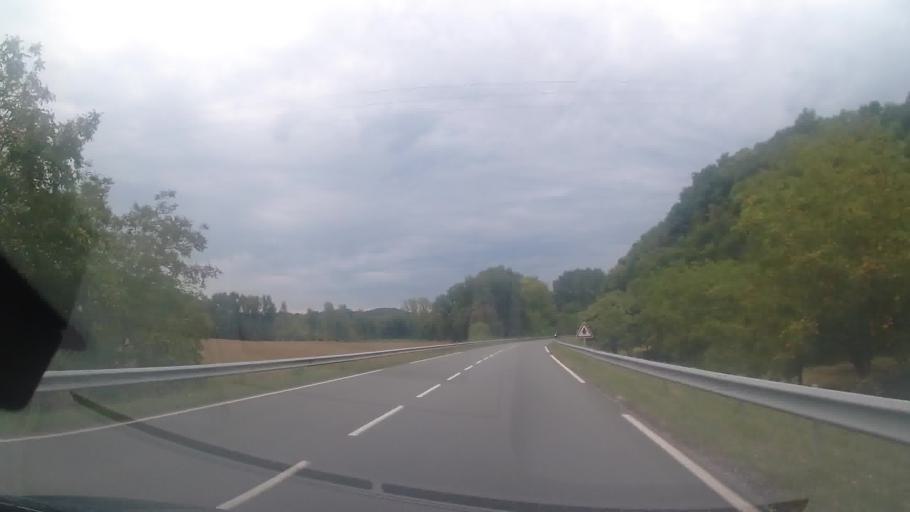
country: FR
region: Aquitaine
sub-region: Departement de la Dordogne
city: Carsac-Aillac
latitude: 44.8470
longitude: 1.3106
